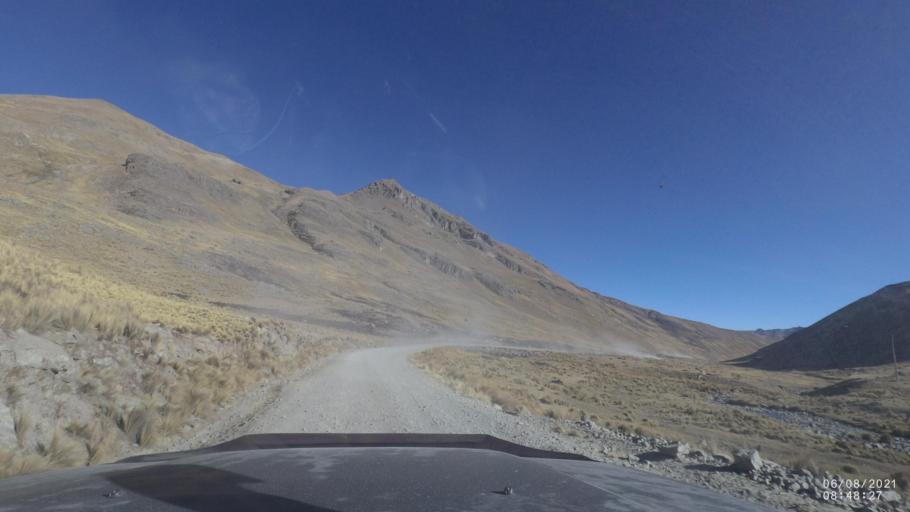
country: BO
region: Cochabamba
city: Sipe Sipe
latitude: -17.1623
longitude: -66.4293
